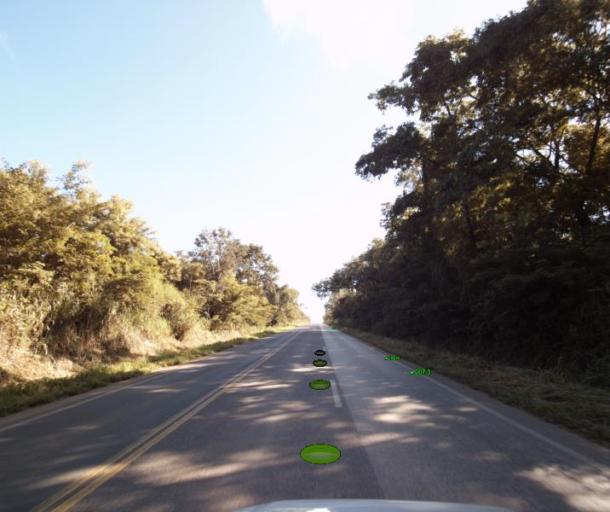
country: BR
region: Goias
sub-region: Uruacu
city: Uruacu
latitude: -14.5894
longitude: -49.1620
